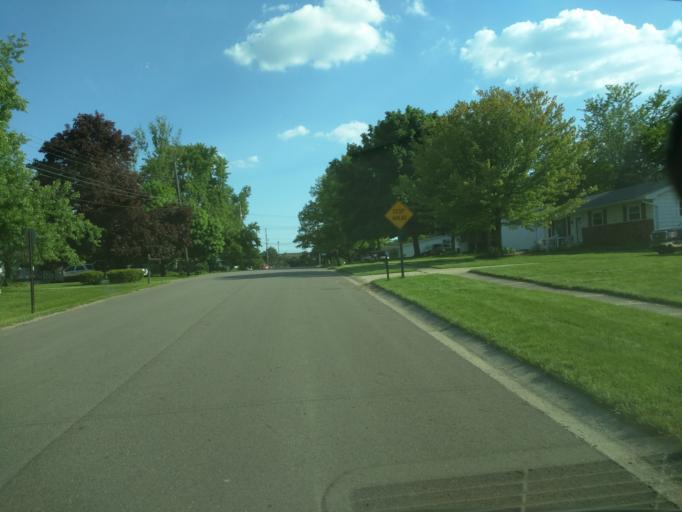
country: US
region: Michigan
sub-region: Eaton County
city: Waverly
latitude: 42.7283
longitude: -84.6055
